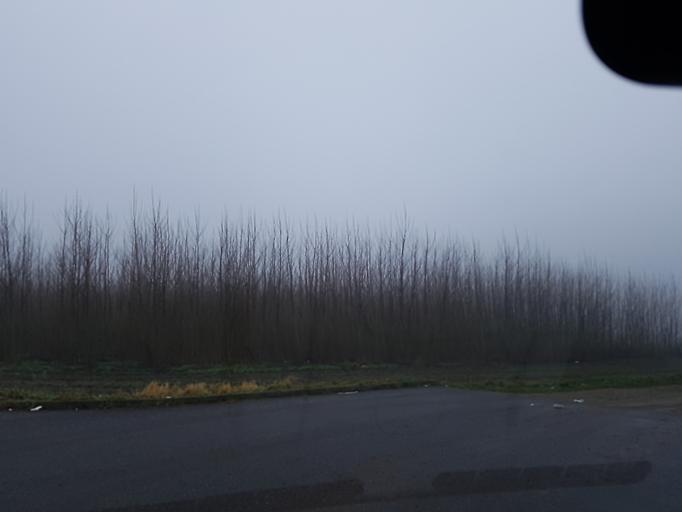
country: DE
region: Brandenburg
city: Finsterwalde
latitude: 51.6282
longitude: 13.7413
